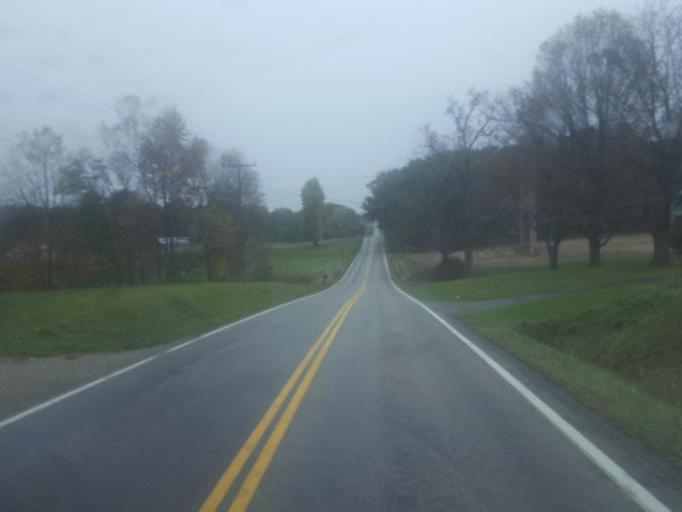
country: US
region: Ohio
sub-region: Ashland County
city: Ashland
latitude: 40.7918
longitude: -82.3397
